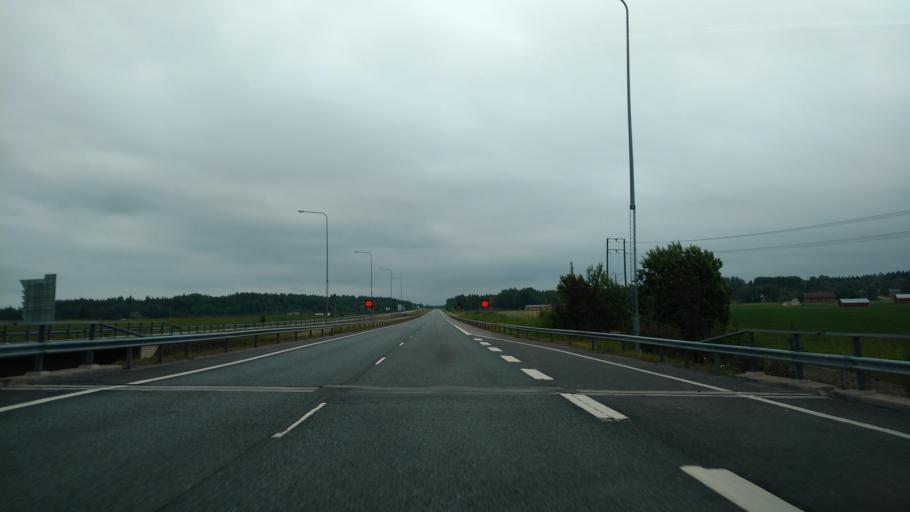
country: FI
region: Varsinais-Suomi
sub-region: Salo
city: Salo
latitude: 60.4150
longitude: 23.1778
